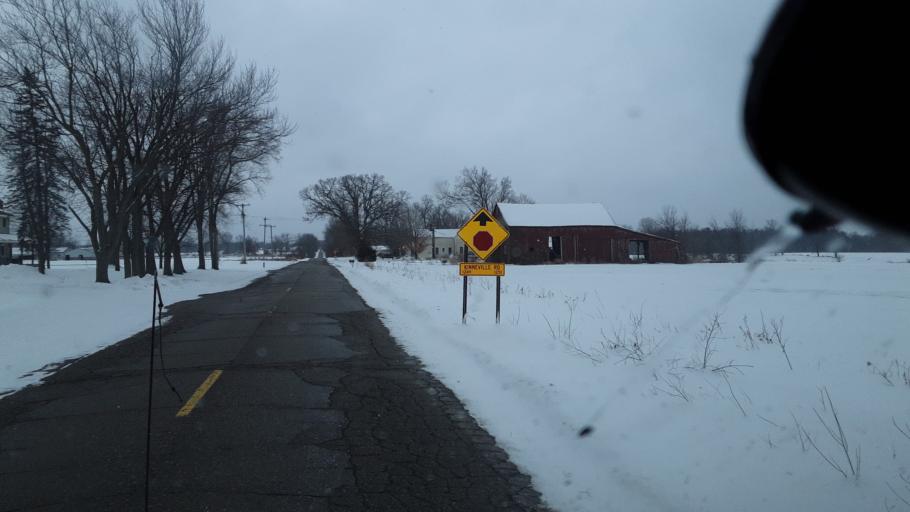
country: US
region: Michigan
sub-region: Ingham County
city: Leslie
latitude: 42.4674
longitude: -84.3941
